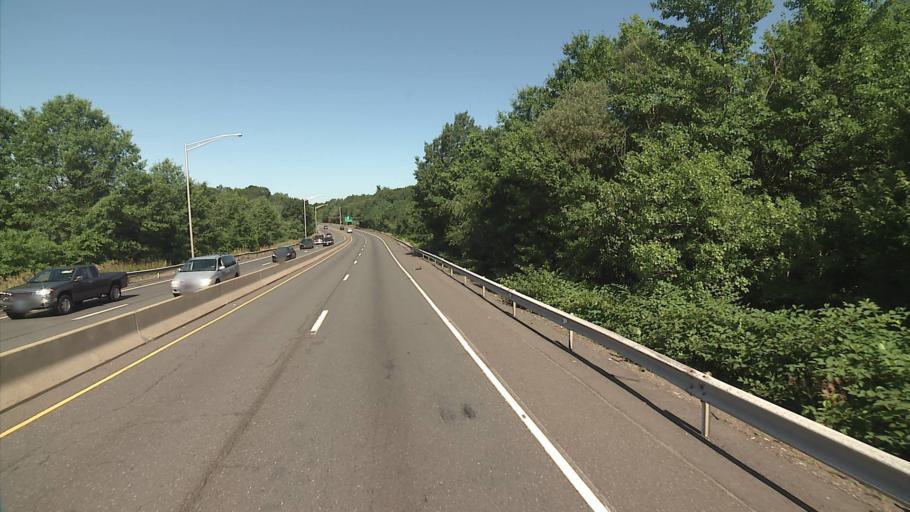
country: US
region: Connecticut
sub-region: Hartford County
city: Plainville
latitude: 41.6781
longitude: -72.8692
